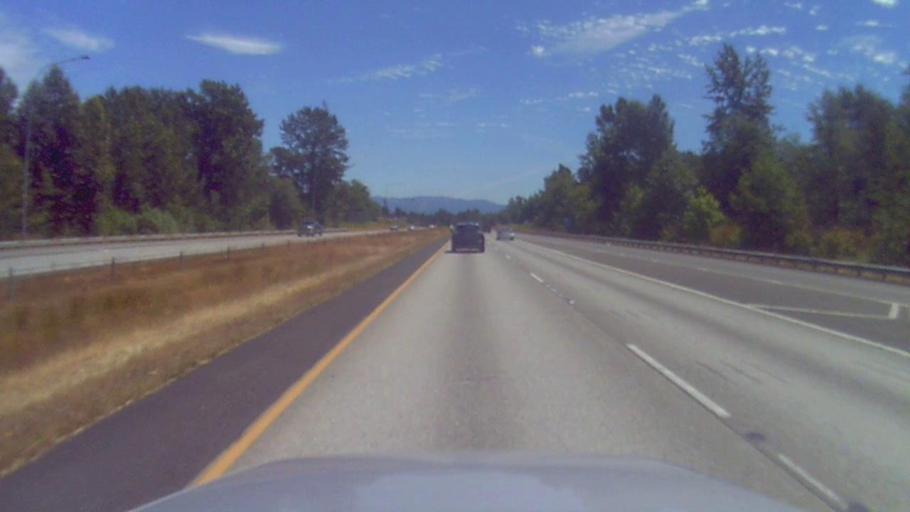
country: US
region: Washington
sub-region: Whatcom County
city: Bellingham
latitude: 48.7870
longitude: -122.5125
